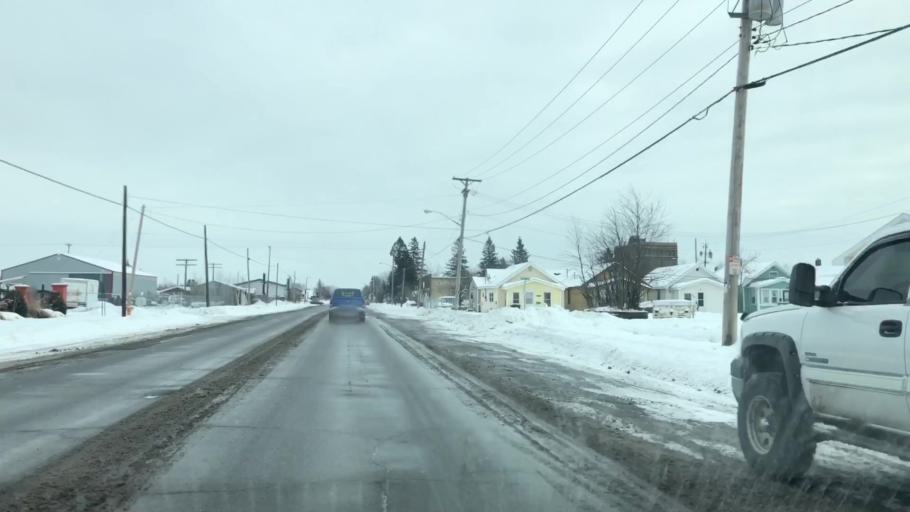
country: US
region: Wisconsin
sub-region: Douglas County
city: Superior
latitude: 46.7279
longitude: -92.1016
